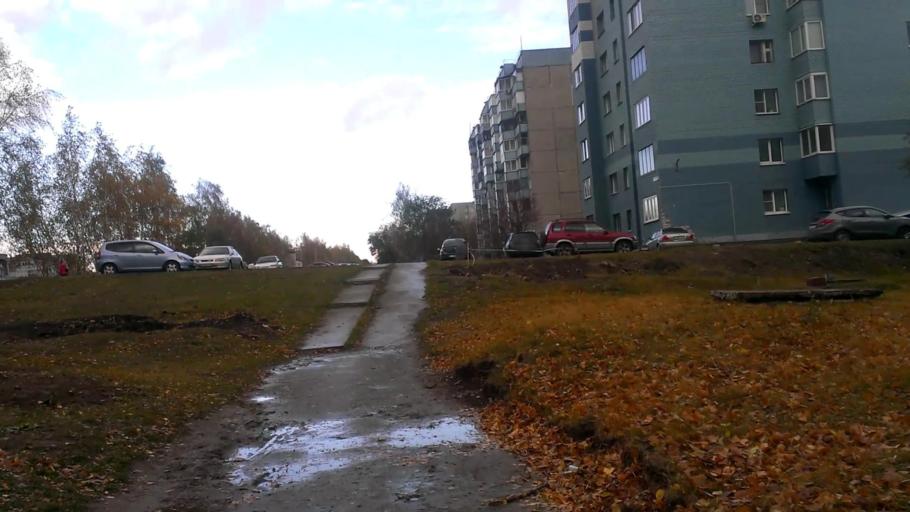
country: RU
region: Altai Krai
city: Novosilikatnyy
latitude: 53.3500
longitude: 83.6732
